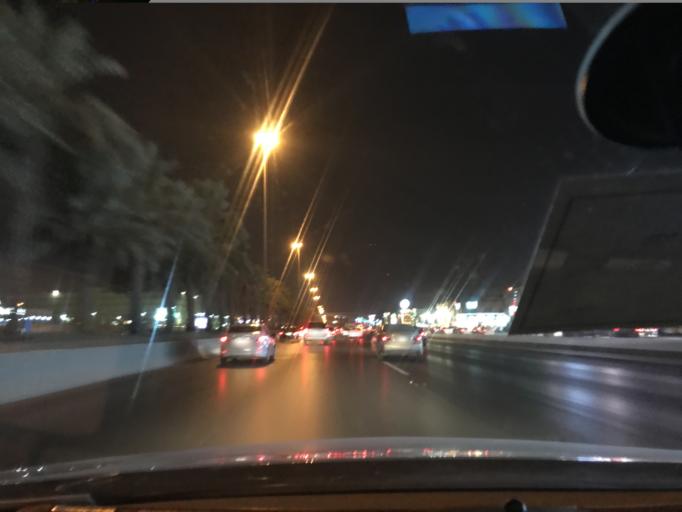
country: SA
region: Ar Riyad
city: Riyadh
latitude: 24.7540
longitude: 46.7419
